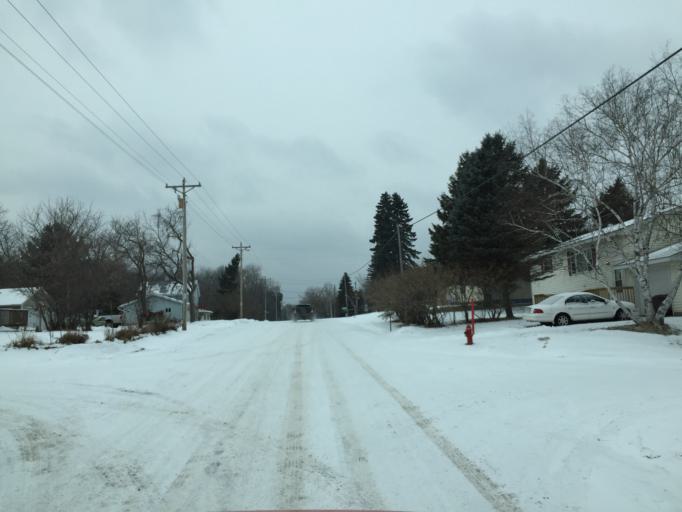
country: US
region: Minnesota
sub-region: Mille Lacs County
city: Vineland
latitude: 46.0687
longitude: -93.6740
